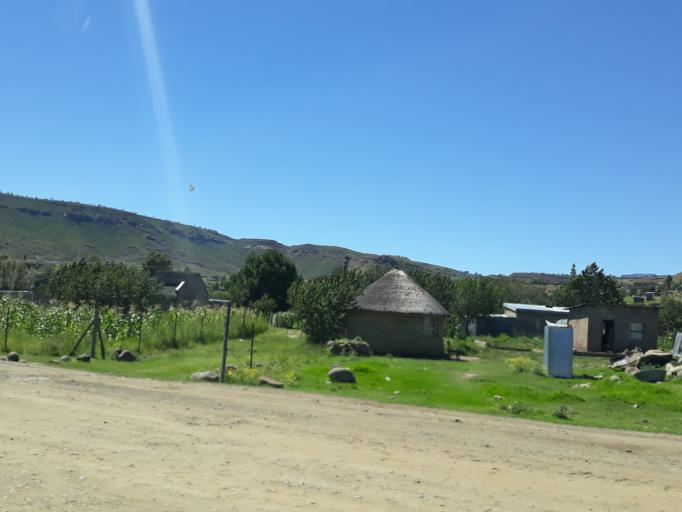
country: LS
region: Mohale's Hoek District
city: Mohale's Hoek
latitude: -30.1112
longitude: 27.4698
